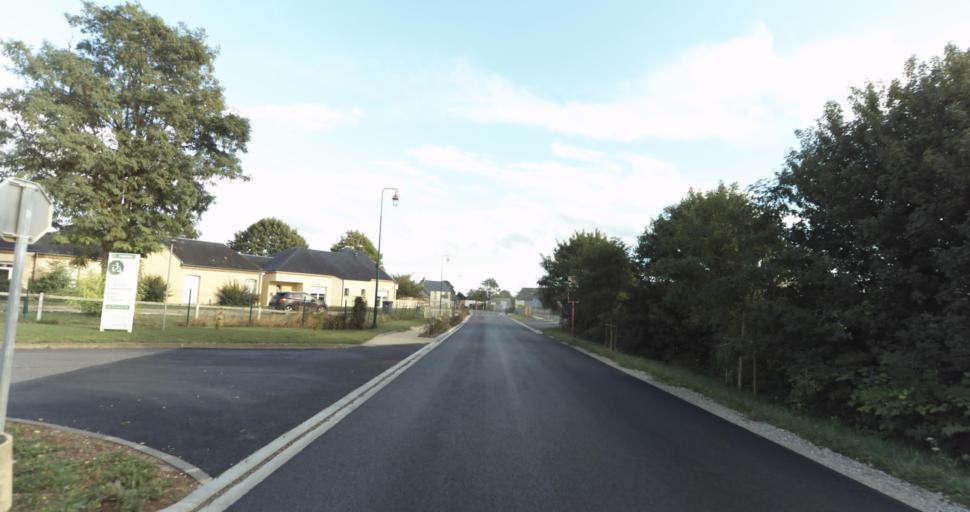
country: FR
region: Lower Normandy
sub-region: Departement de l'Orne
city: Sainte-Gauburge-Sainte-Colombe
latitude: 48.7434
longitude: 0.3859
